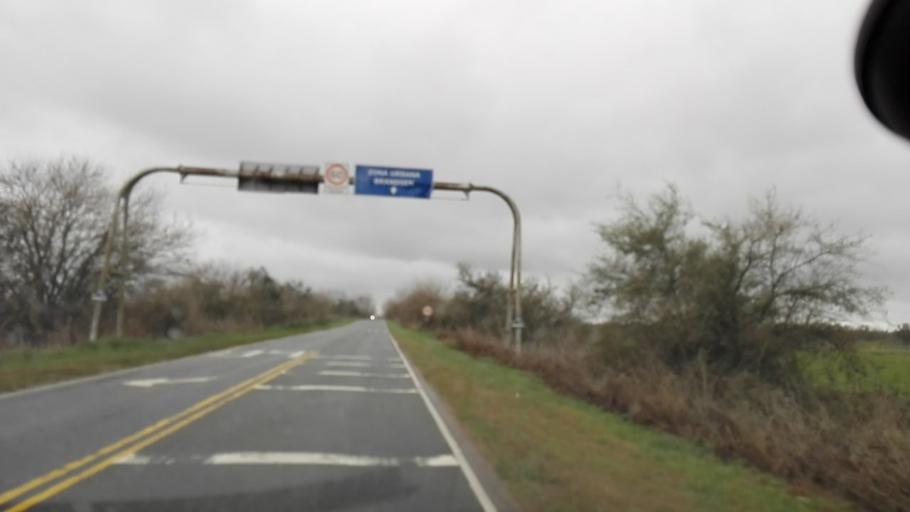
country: AR
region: Buenos Aires
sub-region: Partido de Brandsen
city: Brandsen
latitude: -35.1805
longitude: -58.2597
